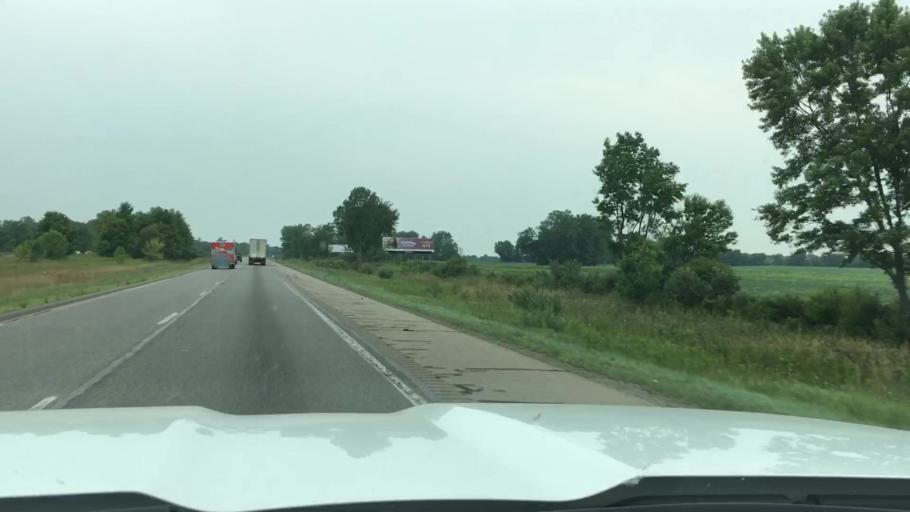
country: US
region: Michigan
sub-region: Ingham County
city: Williamston
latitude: 42.6674
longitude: -84.3432
